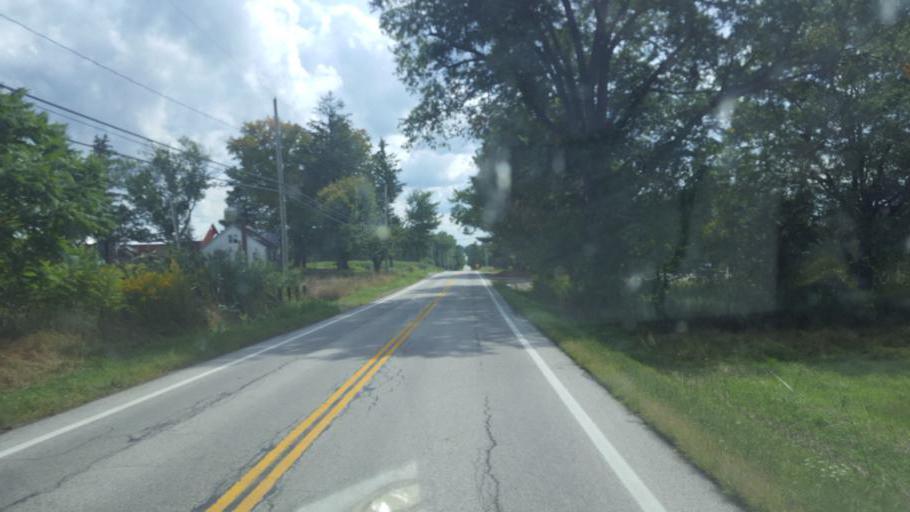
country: US
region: Ohio
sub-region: Portage County
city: Hiram
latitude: 41.3776
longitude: -81.1431
